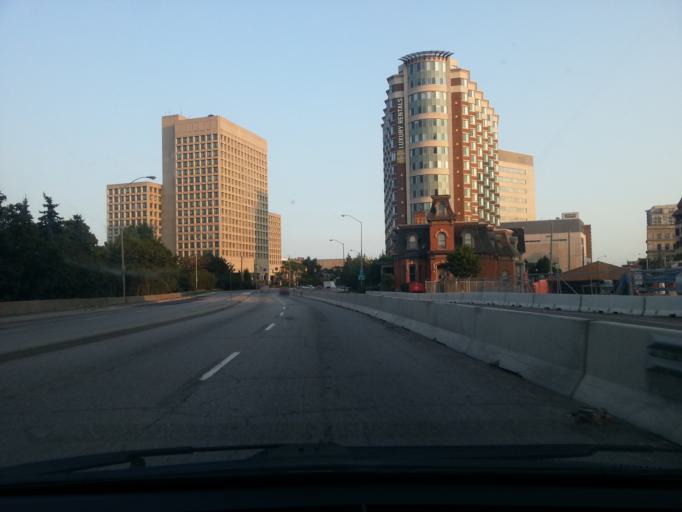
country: CA
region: Ontario
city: Ottawa
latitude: 45.4221
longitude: -75.6855
